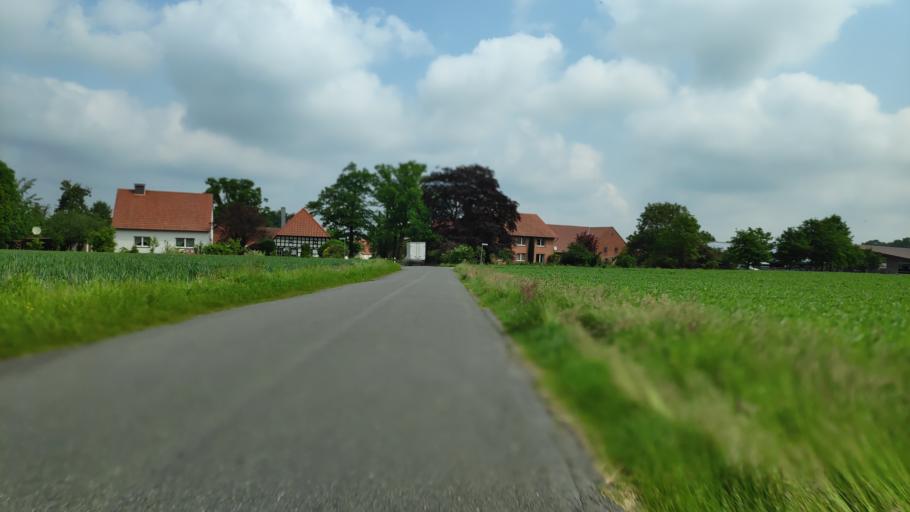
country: DE
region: North Rhine-Westphalia
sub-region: Regierungsbezirk Detmold
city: Hille
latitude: 52.3505
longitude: 8.7632
